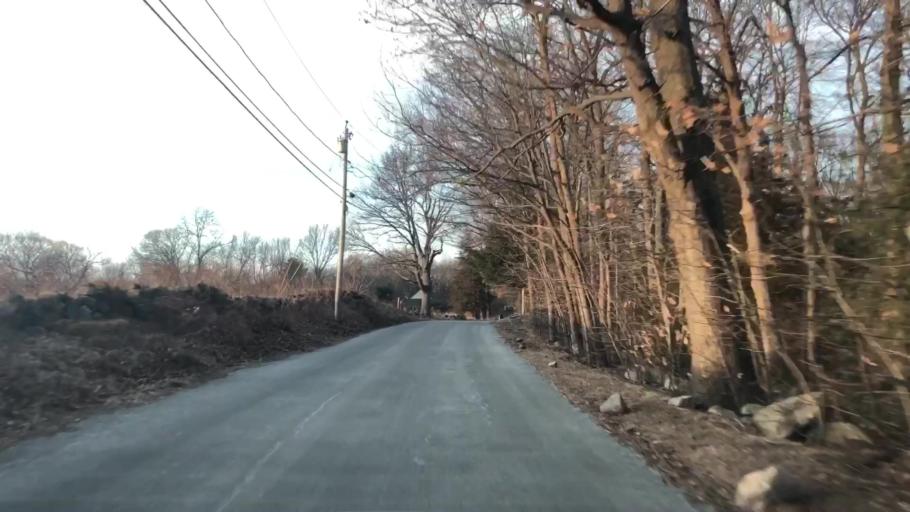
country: US
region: Massachusetts
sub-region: Essex County
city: North Andover
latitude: 42.6918
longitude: -71.0758
